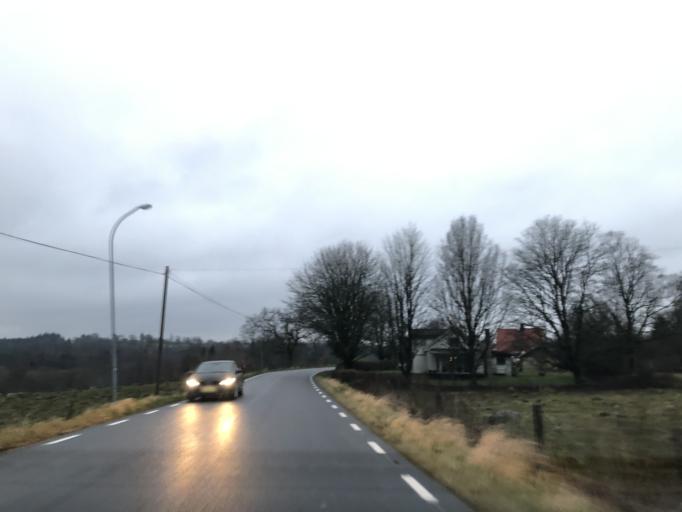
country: SE
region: Vaestra Goetaland
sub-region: Boras Kommun
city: Dalsjofors
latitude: 57.8392
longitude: 13.2244
